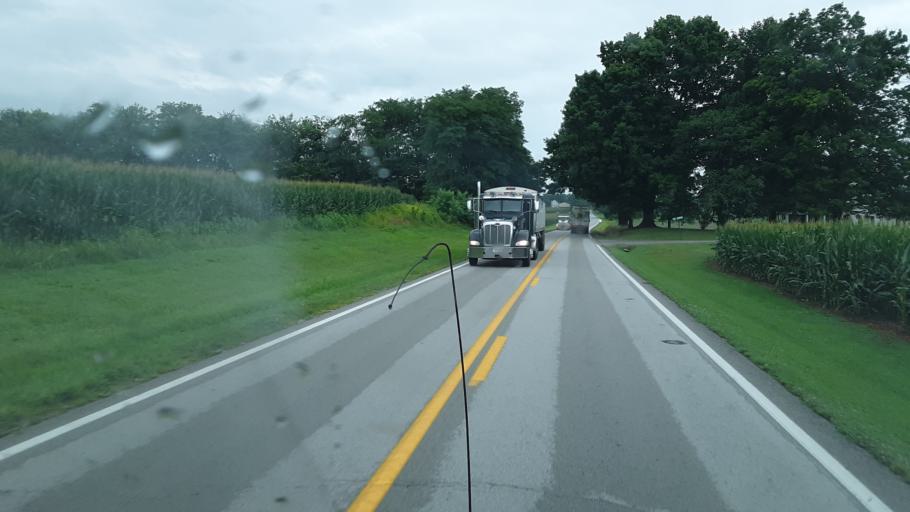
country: US
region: Kentucky
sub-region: Todd County
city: Elkton
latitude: 36.7582
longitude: -87.0323
